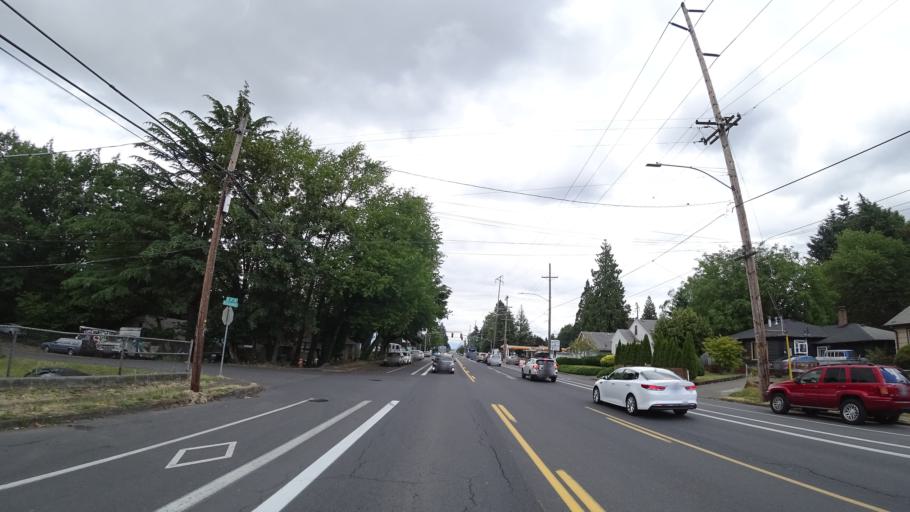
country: US
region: Oregon
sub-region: Multnomah County
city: Portland
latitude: 45.5628
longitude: -122.6023
